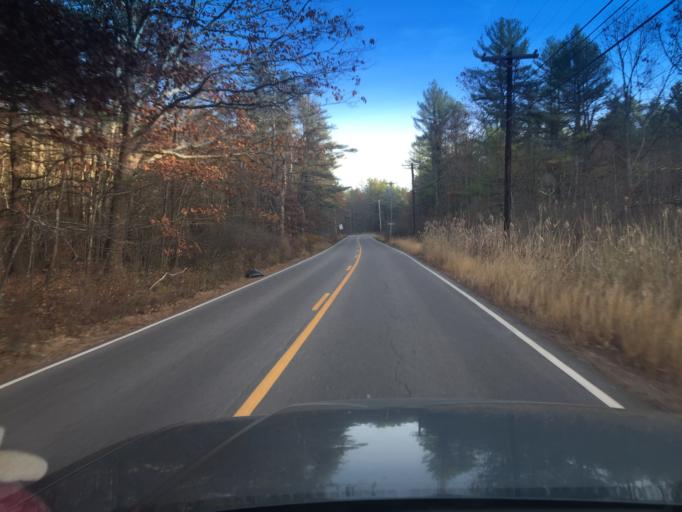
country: US
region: Maine
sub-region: York County
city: Eliot
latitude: 43.1741
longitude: -70.7209
